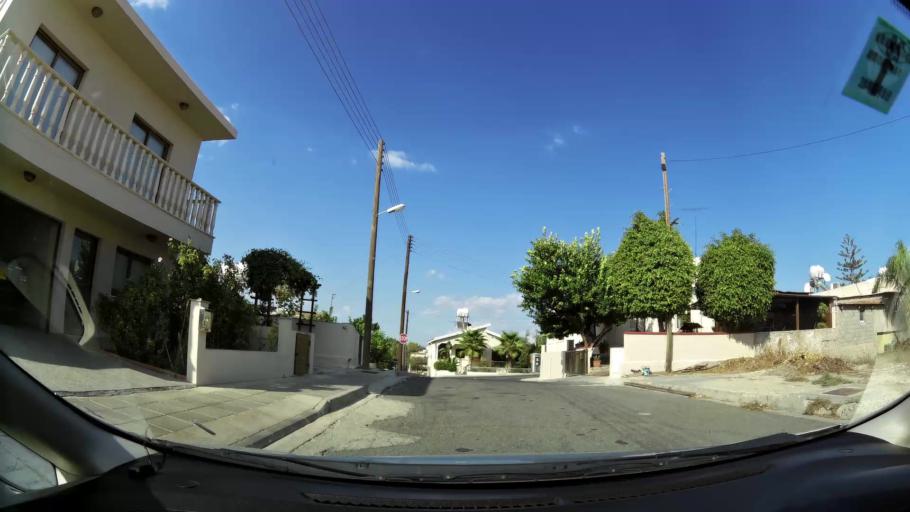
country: CY
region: Larnaka
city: Livadia
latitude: 34.9459
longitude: 33.6220
